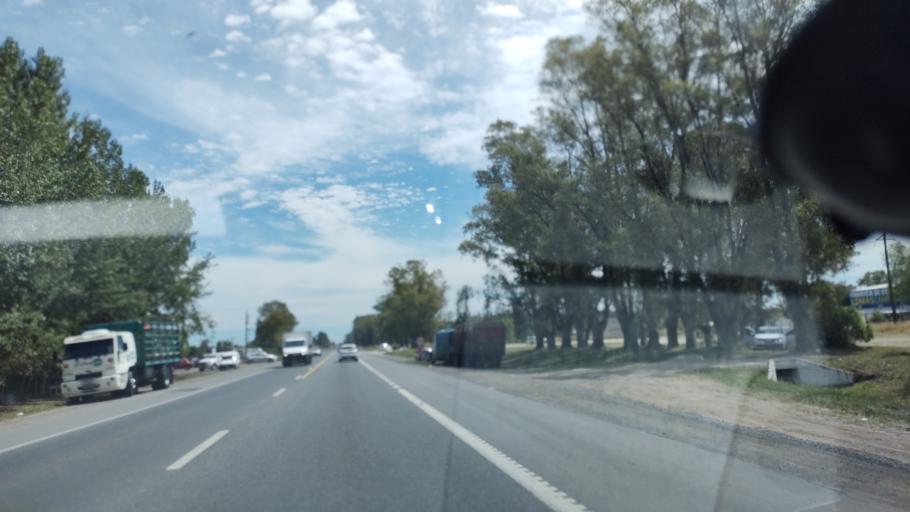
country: AR
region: Buenos Aires
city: Canuelas
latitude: -35.0304
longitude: -58.7498
